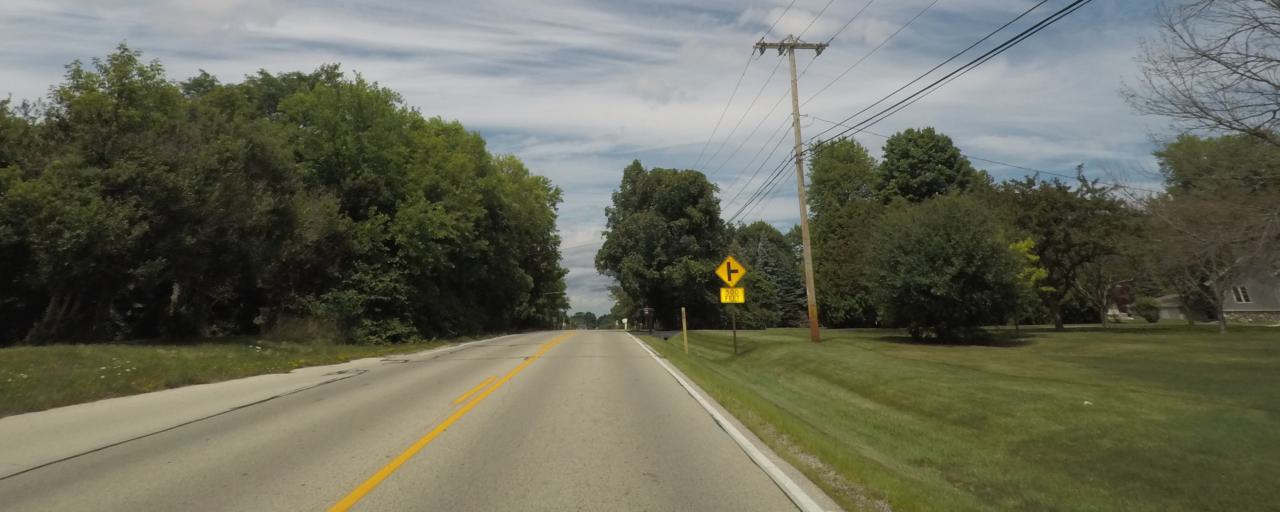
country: US
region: Wisconsin
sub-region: Waukesha County
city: New Berlin
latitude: 42.9763
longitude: -88.0688
